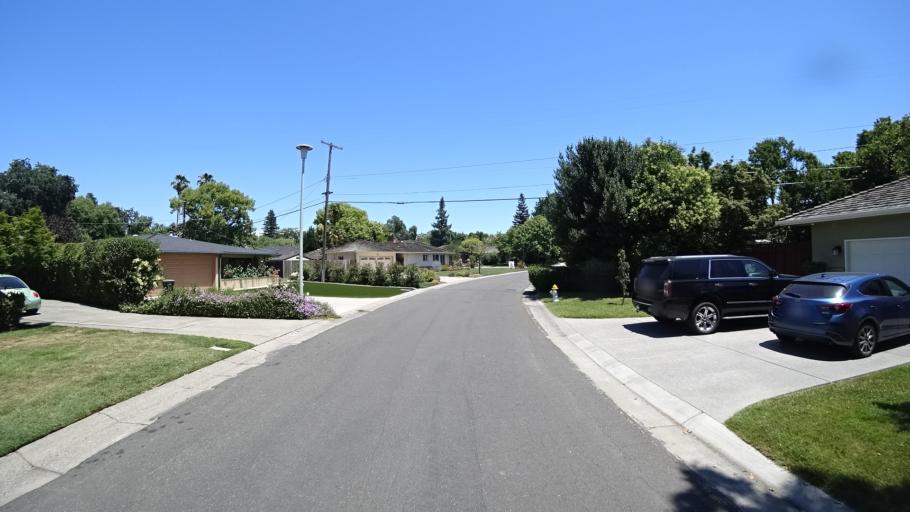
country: US
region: California
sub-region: Sacramento County
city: Sacramento
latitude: 38.5347
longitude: -121.5083
